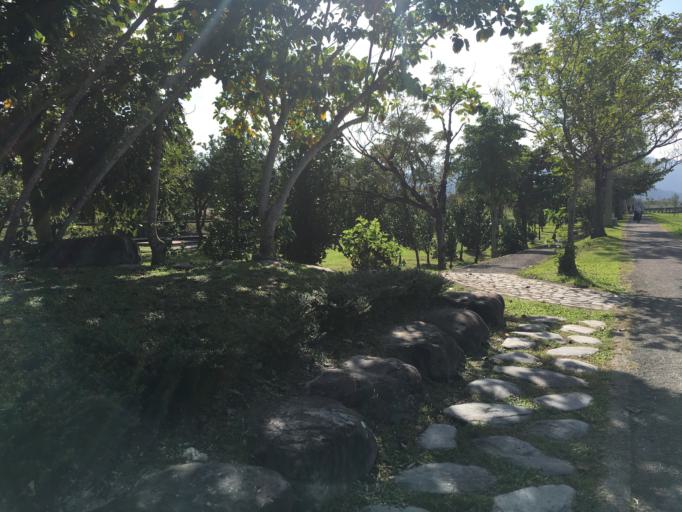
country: TW
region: Taiwan
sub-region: Yilan
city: Yilan
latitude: 24.6861
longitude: 121.7267
